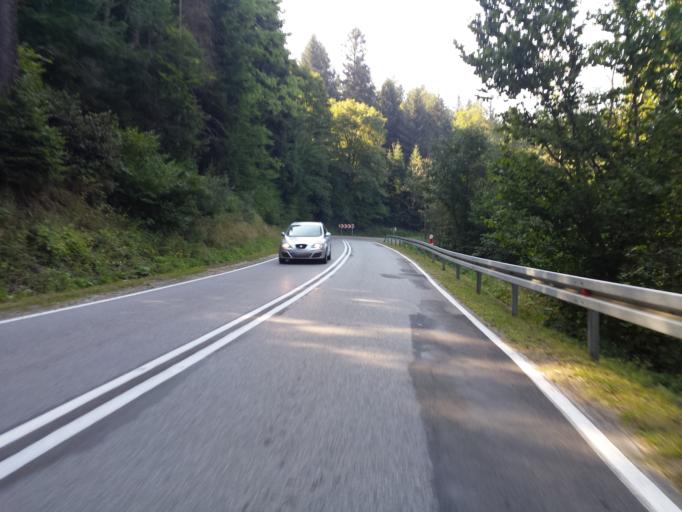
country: PL
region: Subcarpathian Voivodeship
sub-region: Powiat leski
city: Cisna
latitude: 49.2492
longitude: 22.2878
